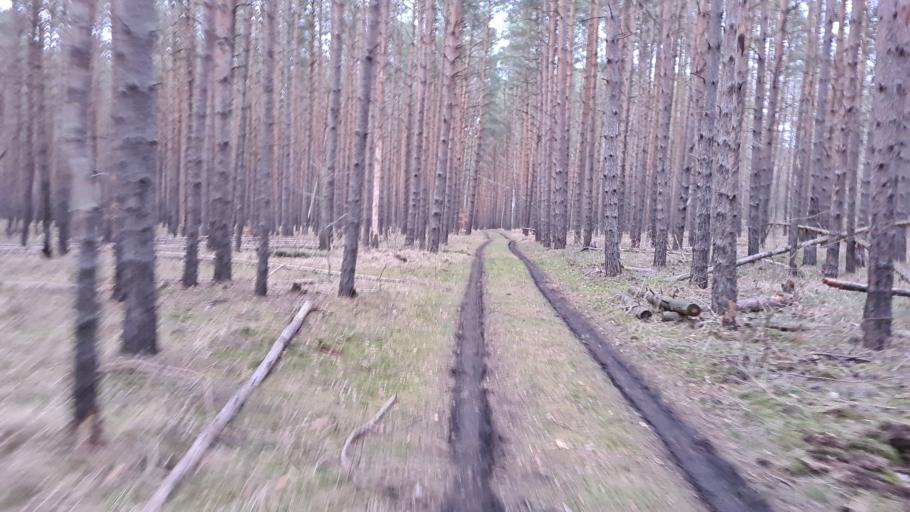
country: DE
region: Brandenburg
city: Trobitz
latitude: 51.5937
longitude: 13.4581
